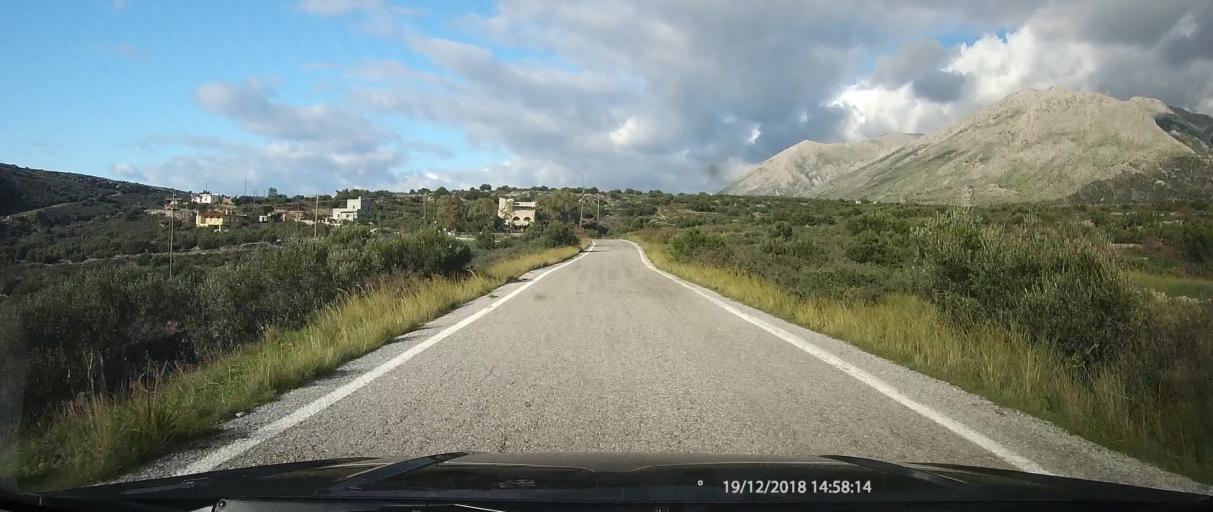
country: GR
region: Peloponnese
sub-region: Nomos Lakonias
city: Gytheio
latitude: 36.4869
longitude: 22.4027
